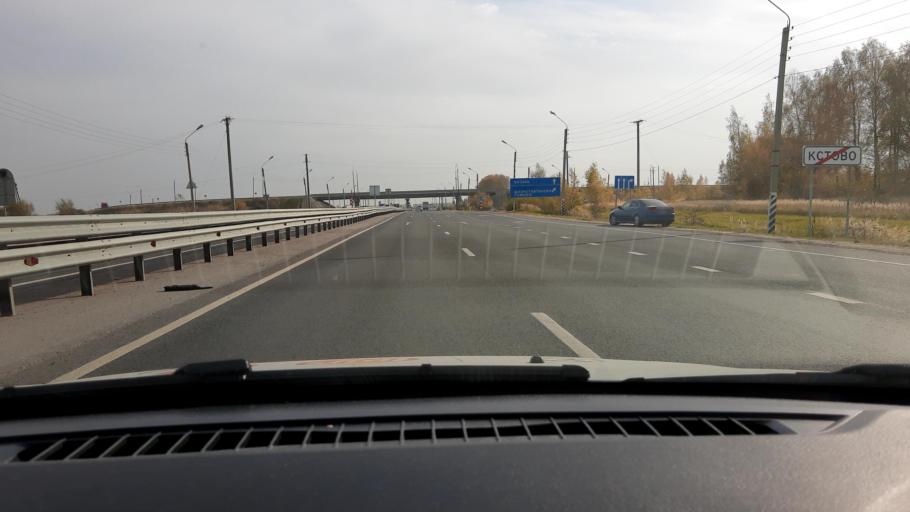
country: RU
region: Nizjnij Novgorod
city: Kstovo
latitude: 56.1291
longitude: 44.2574
